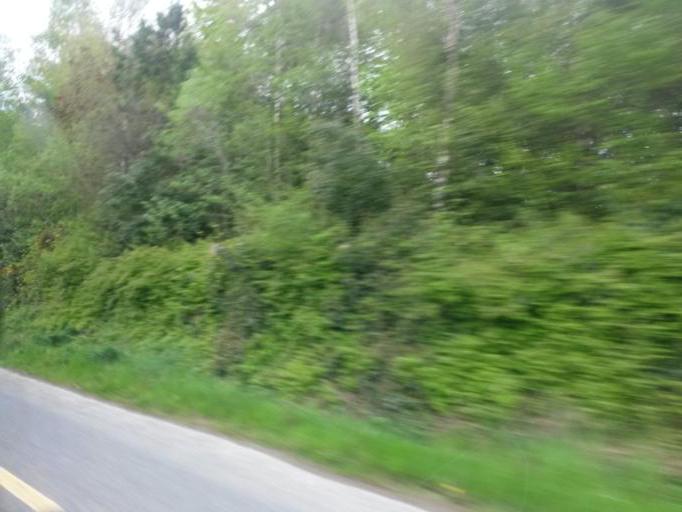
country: IE
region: Leinster
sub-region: Loch Garman
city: Enniscorthy
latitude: 52.4412
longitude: -6.5396
